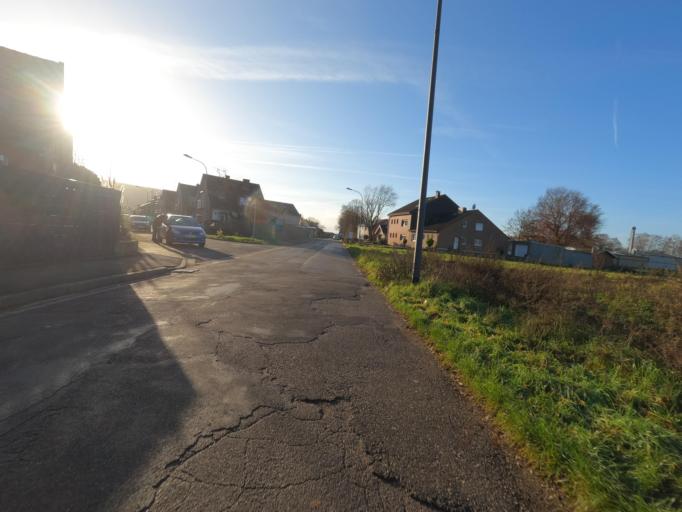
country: DE
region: North Rhine-Westphalia
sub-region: Regierungsbezirk Koln
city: Titz
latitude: 50.9547
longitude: 6.4271
